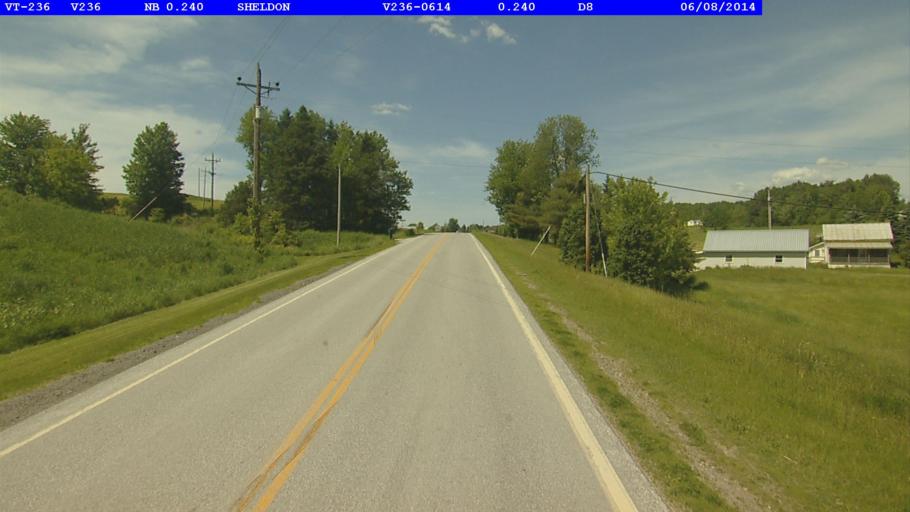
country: US
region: Vermont
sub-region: Franklin County
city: Enosburg Falls
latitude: 44.9145
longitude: -72.8648
